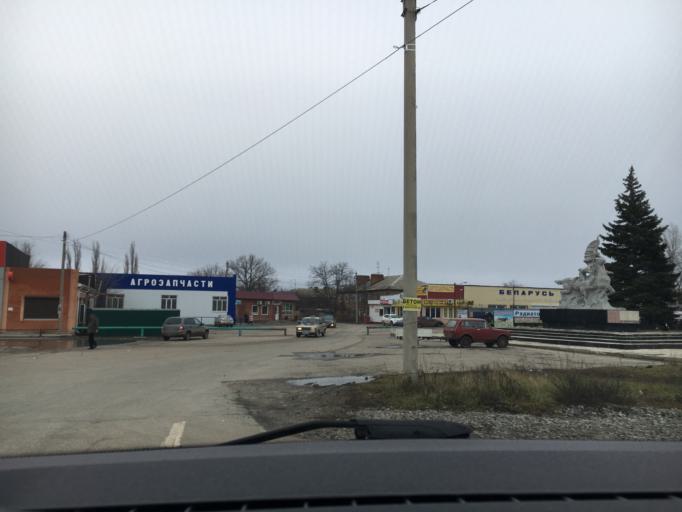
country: RU
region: Rostov
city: Yegorlykskaya
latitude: 46.5525
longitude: 40.6472
